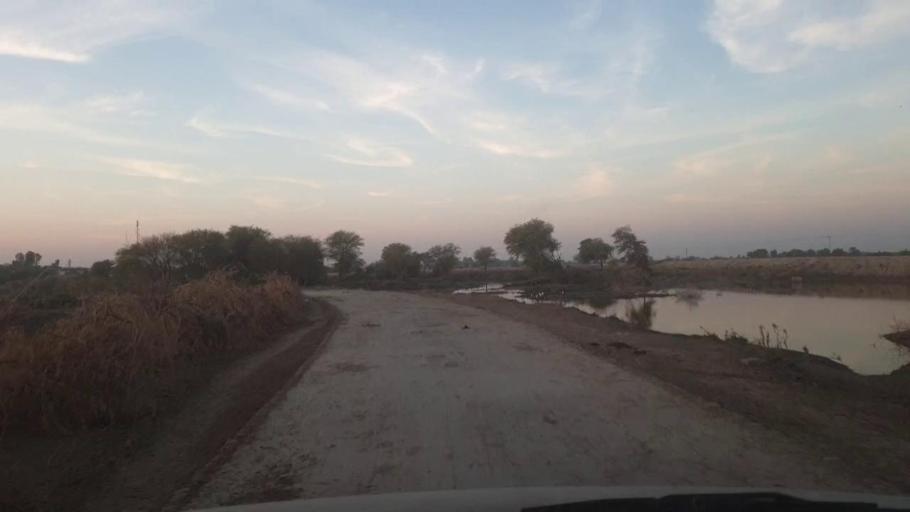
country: PK
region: Sindh
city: Hala
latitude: 25.7004
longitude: 68.3021
